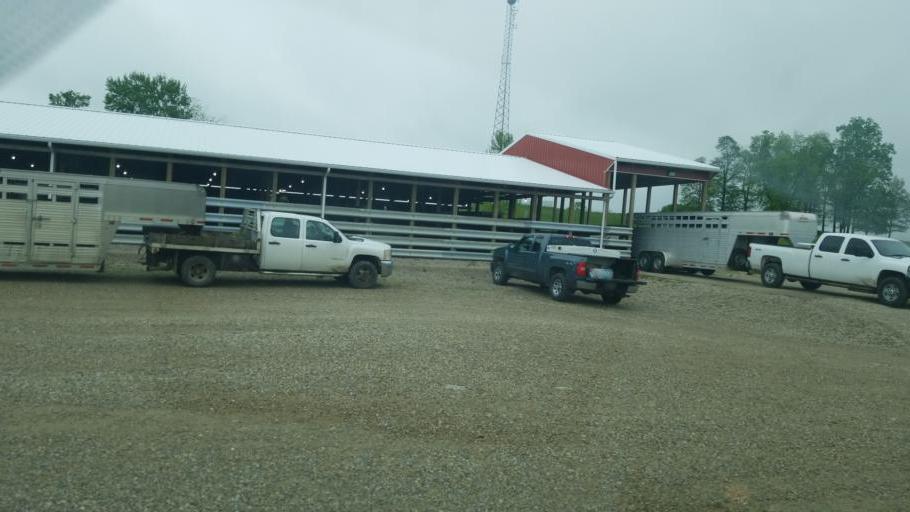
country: US
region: Ohio
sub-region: Highland County
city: Hillsboro
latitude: 39.2164
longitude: -83.5937
